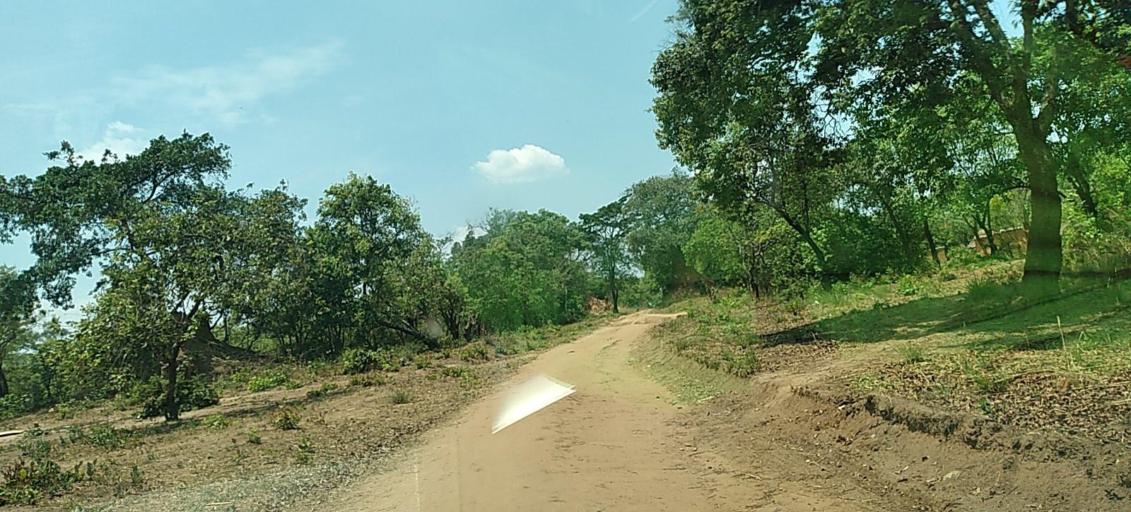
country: CD
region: Katanga
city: Kolwezi
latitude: -11.3202
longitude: 25.2301
